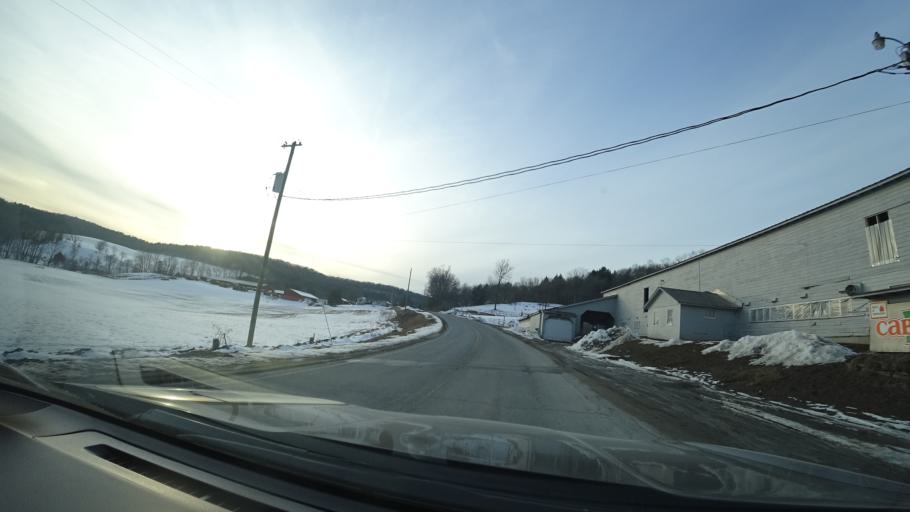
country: US
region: New York
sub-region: Washington County
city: Greenwich
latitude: 43.1891
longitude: -73.3723
